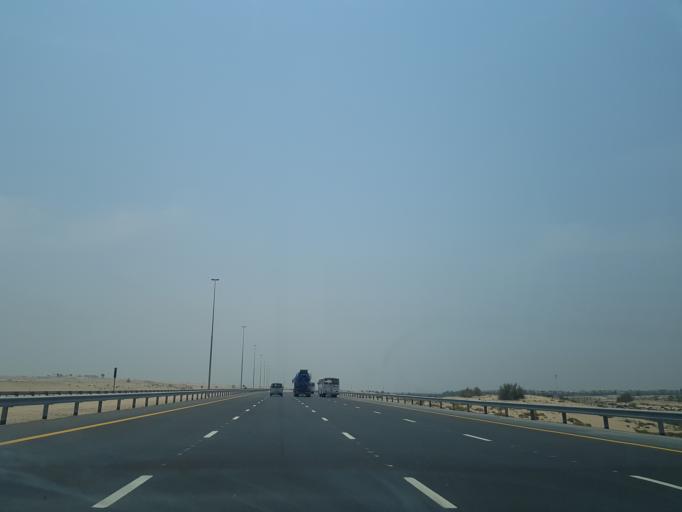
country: AE
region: Dubai
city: Dubai
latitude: 25.0152
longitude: 55.2232
